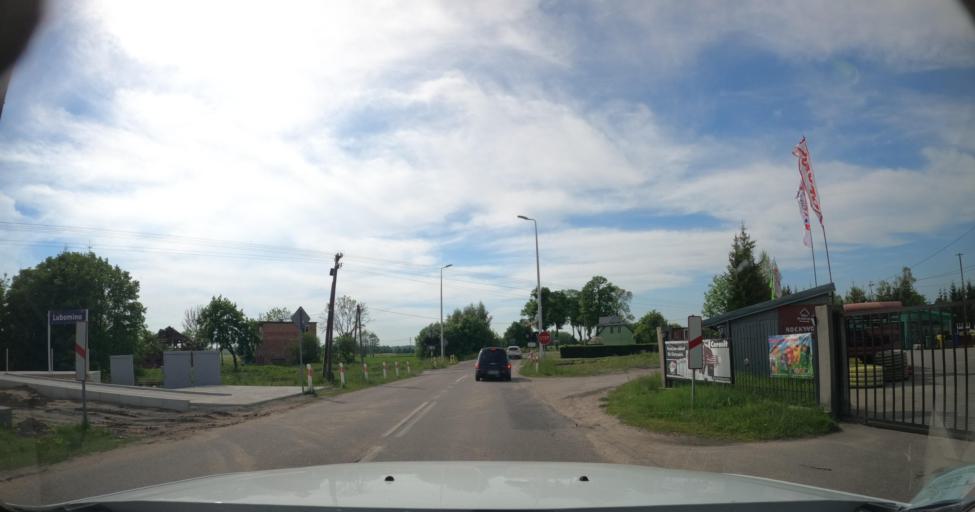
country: PL
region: Warmian-Masurian Voivodeship
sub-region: Powiat lidzbarski
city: Lubomino
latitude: 54.0671
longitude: 20.2328
